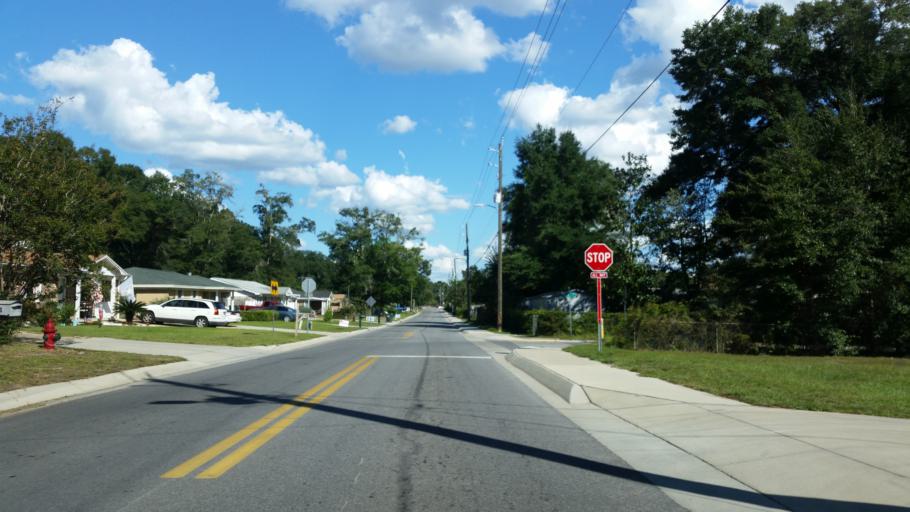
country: US
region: Florida
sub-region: Santa Rosa County
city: Milton
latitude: 30.6382
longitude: -87.0535
